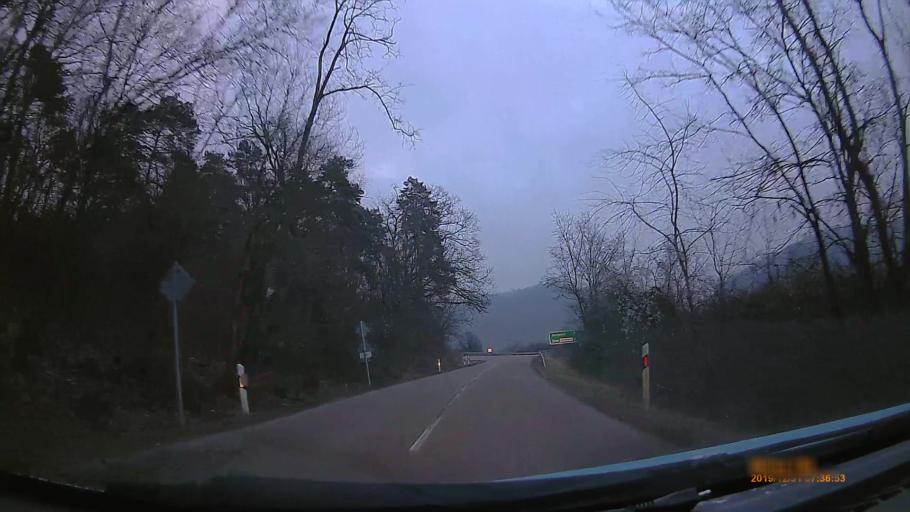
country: HU
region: Heves
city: Sirok
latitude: 47.9212
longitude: 20.1754
